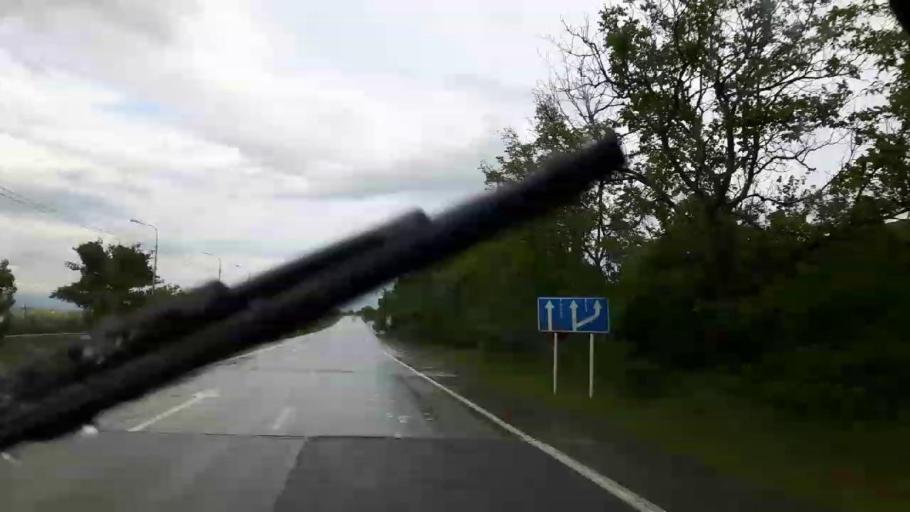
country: GE
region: Shida Kartli
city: Kaspi
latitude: 41.9651
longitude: 44.4674
